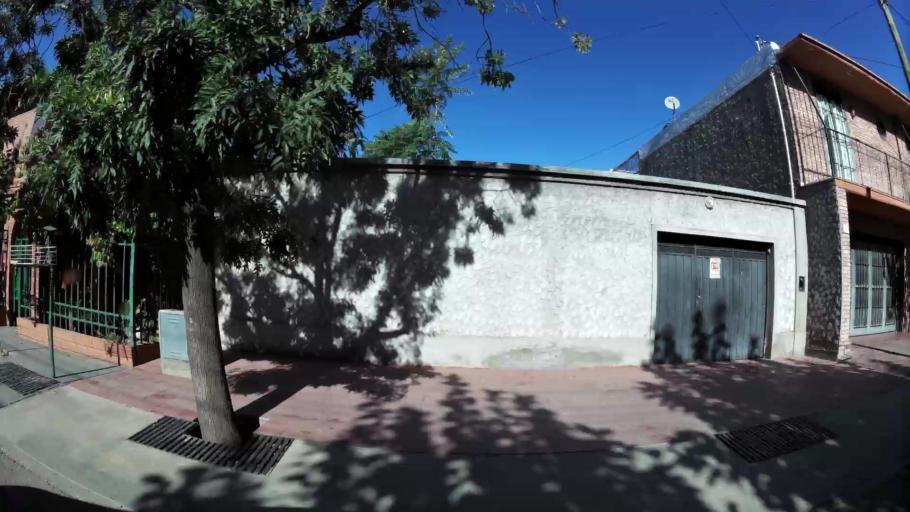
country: AR
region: Mendoza
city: Mendoza
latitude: -32.9059
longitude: -68.8157
